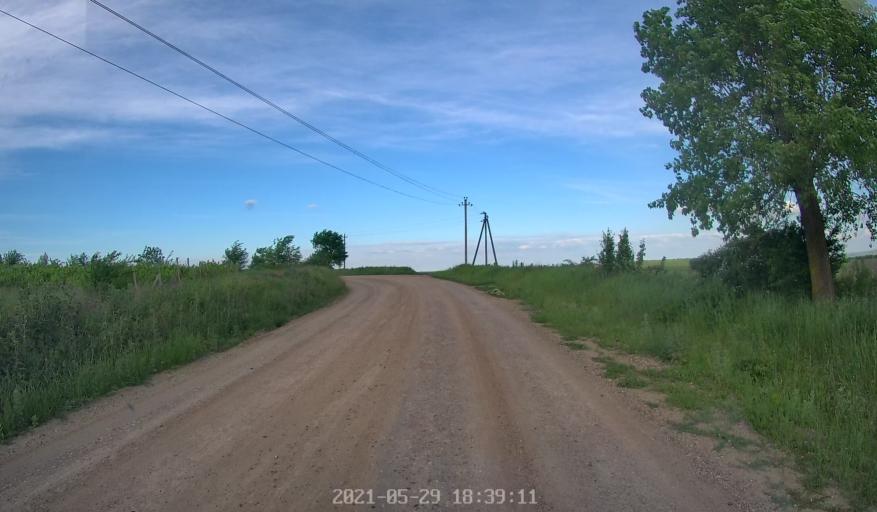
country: MD
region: Chisinau
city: Singera
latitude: 46.8009
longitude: 28.9426
